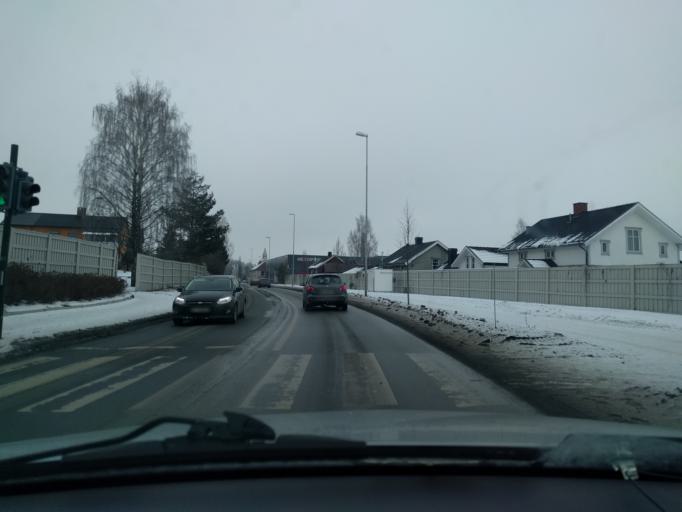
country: NO
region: Hedmark
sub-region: Hamar
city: Hamar
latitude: 60.7964
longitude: 11.0968
